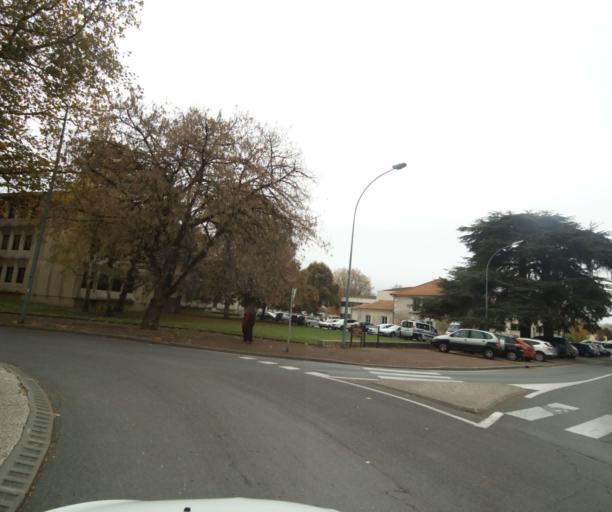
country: FR
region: Poitou-Charentes
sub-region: Departement de la Charente-Maritime
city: Saintes
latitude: 45.7434
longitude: -0.6258
